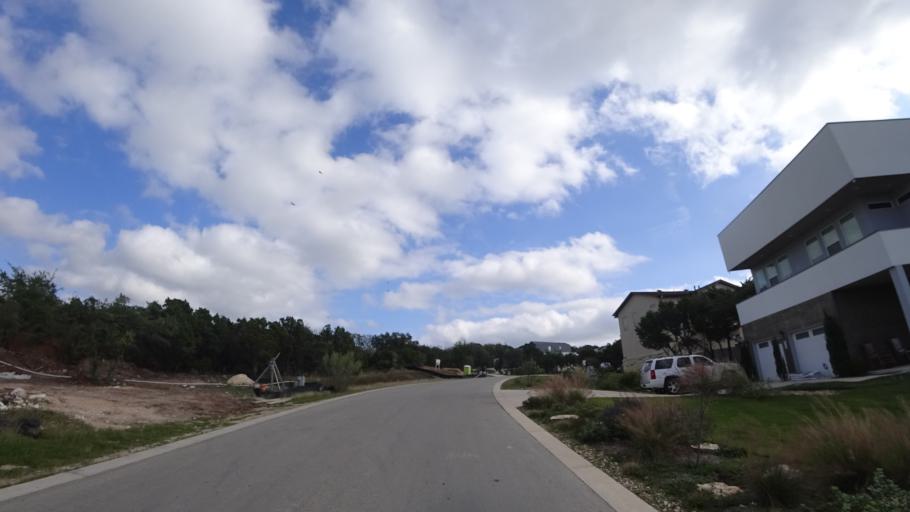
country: US
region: Texas
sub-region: Travis County
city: Bee Cave
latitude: 30.2535
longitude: -97.9260
